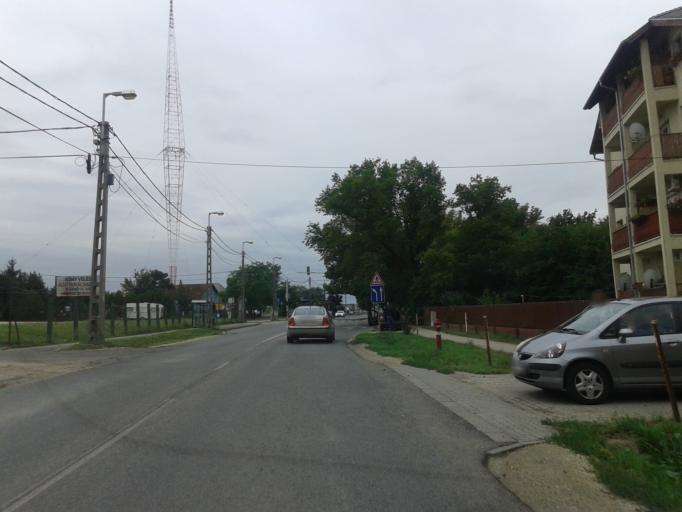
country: HU
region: Pest
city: Halasztelek
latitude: 47.3777
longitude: 19.0076
